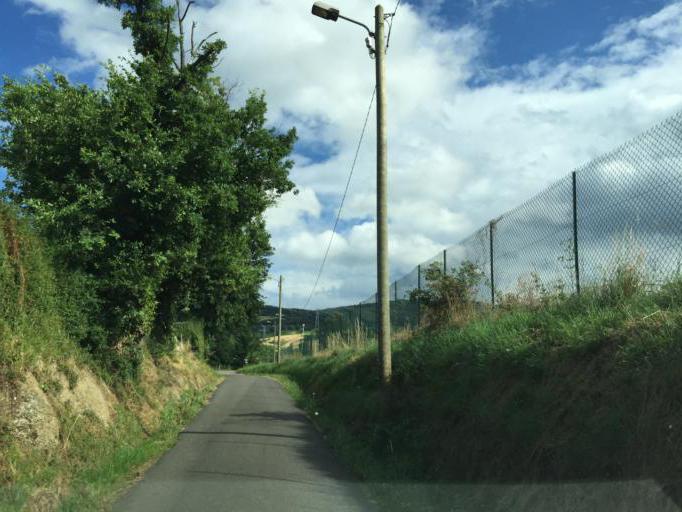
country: FR
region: Rhone-Alpes
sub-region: Departement de la Loire
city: Saint-Jean-Bonnefonds
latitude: 45.4509
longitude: 4.4795
